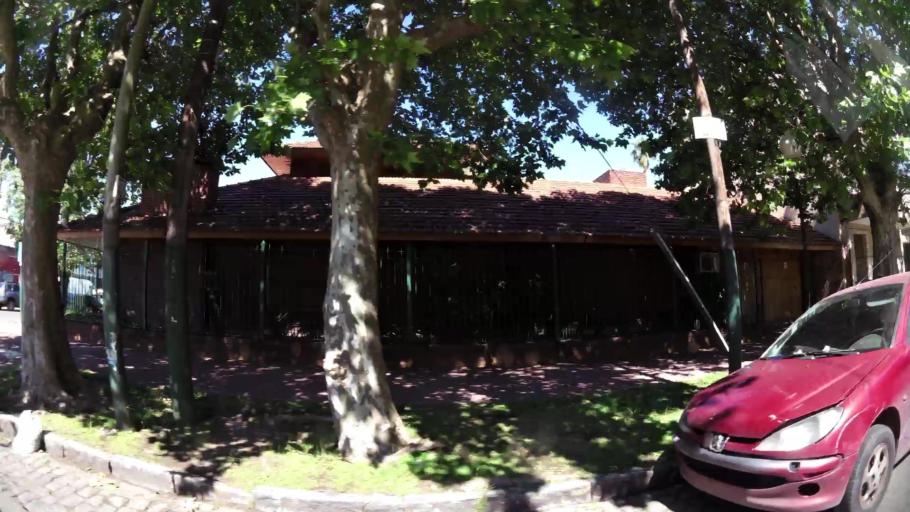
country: AR
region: Buenos Aires
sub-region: Partido de Lomas de Zamora
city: Lomas de Zamora
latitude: -34.7610
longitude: -58.4087
